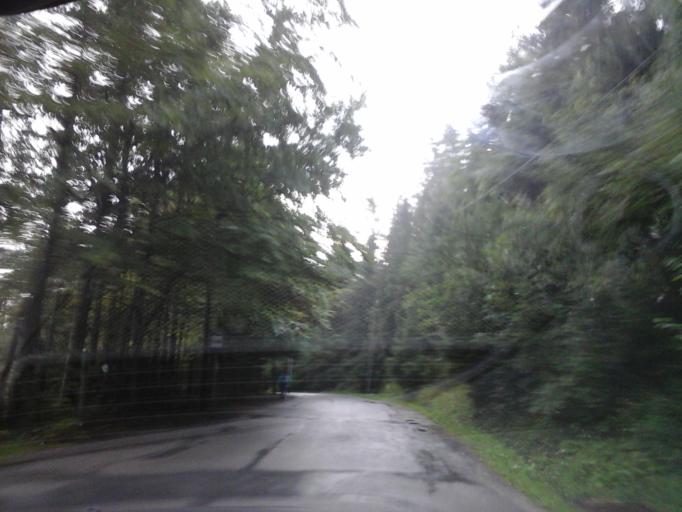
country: PL
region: Lesser Poland Voivodeship
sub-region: Powiat tatrzanski
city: Koscielisko
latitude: 49.2972
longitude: 19.9054
